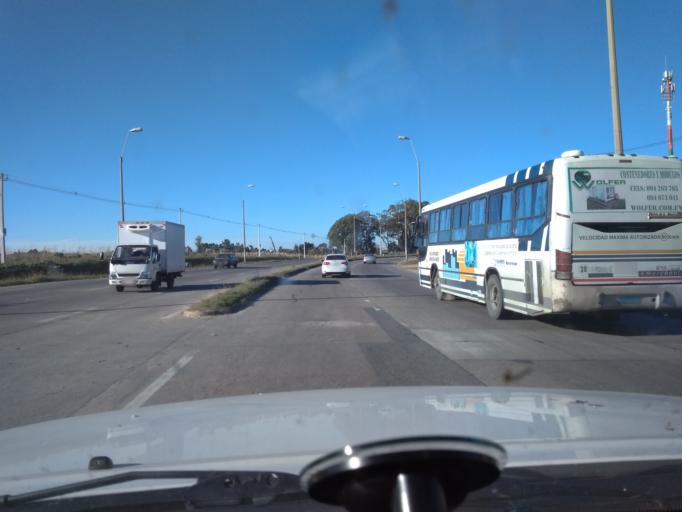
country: UY
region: Canelones
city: Colonia Nicolich
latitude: -34.7762
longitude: -56.0524
